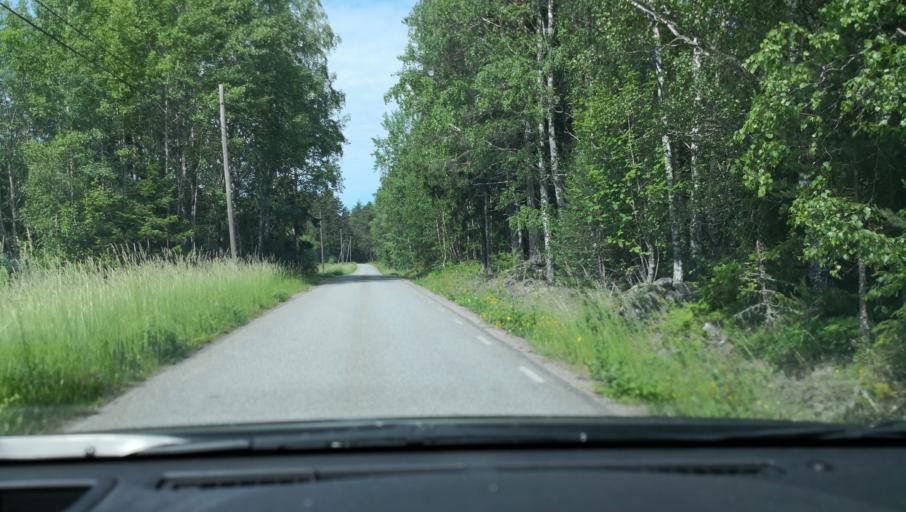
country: SE
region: Stockholm
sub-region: Sigtuna Kommun
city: Sigtuna
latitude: 59.6905
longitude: 17.6477
